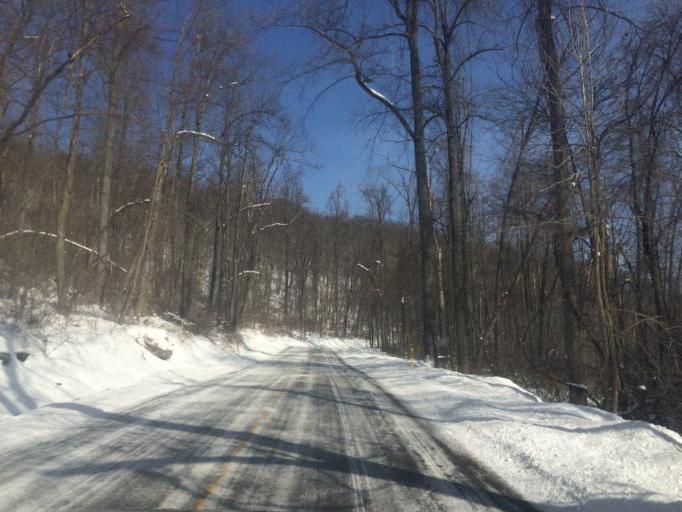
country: US
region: Pennsylvania
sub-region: Centre County
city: Stormstown
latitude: 40.8784
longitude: -78.0174
